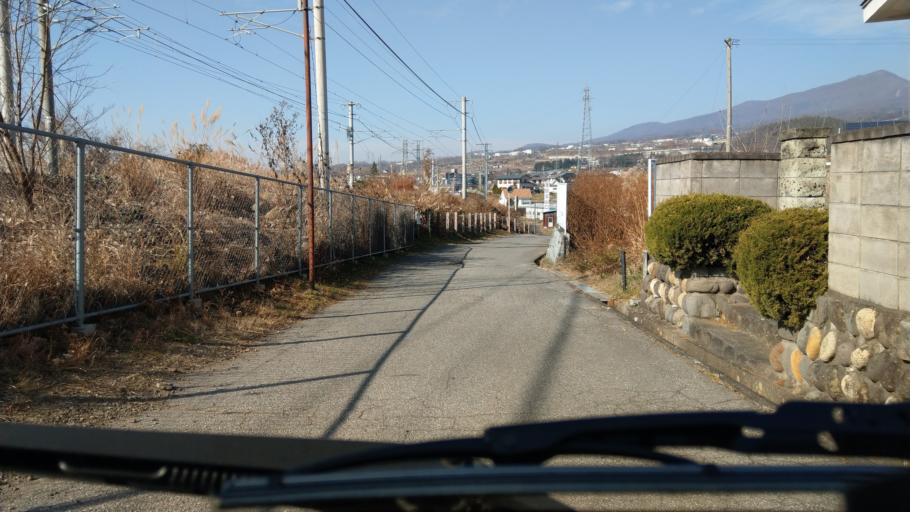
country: JP
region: Nagano
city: Komoro
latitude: 36.3325
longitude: 138.4177
